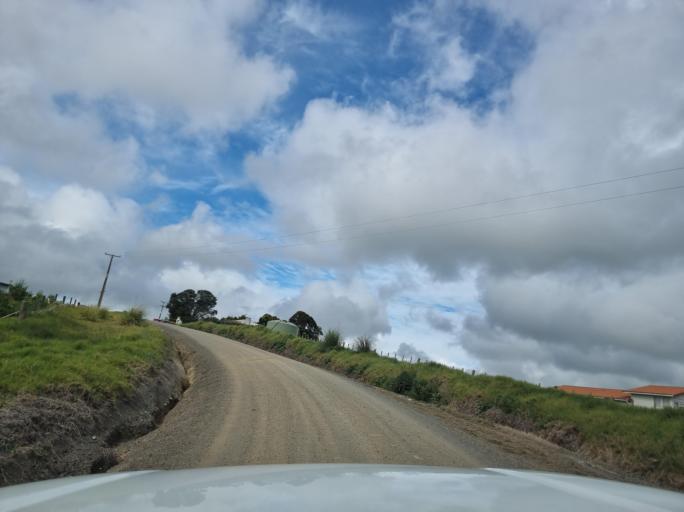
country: NZ
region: Northland
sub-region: Whangarei
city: Ruakaka
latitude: -36.1229
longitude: 174.2086
